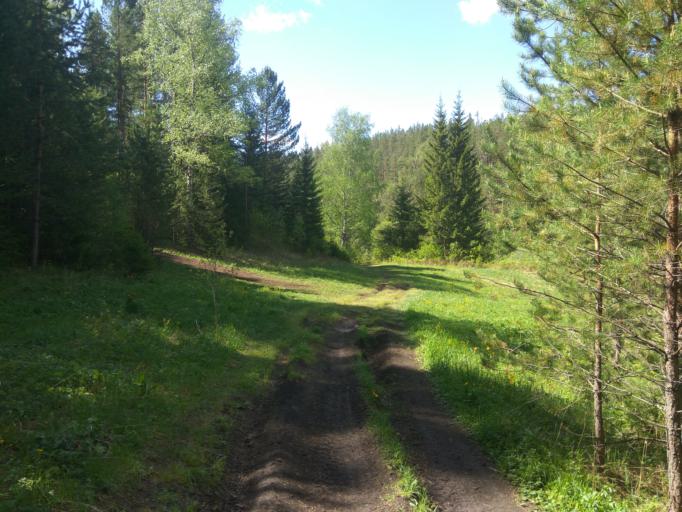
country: RU
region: Krasnoyarskiy
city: Krasnoyarsk
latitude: 55.8986
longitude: 92.9387
